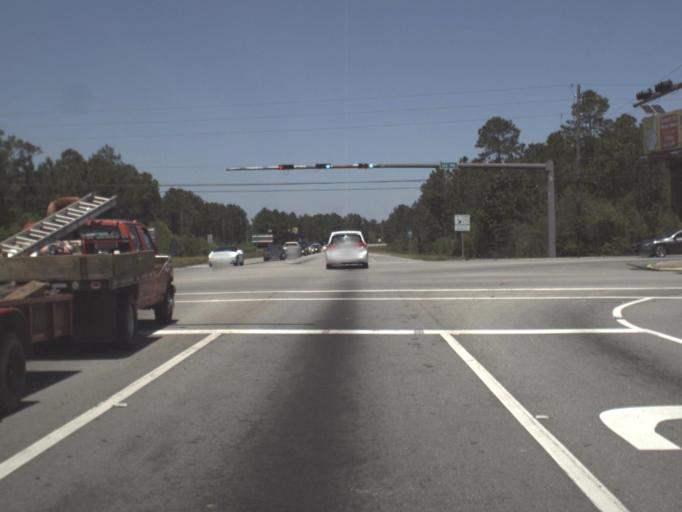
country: US
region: Florida
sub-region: Escambia County
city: Myrtle Grove
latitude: 30.4029
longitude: -87.3424
